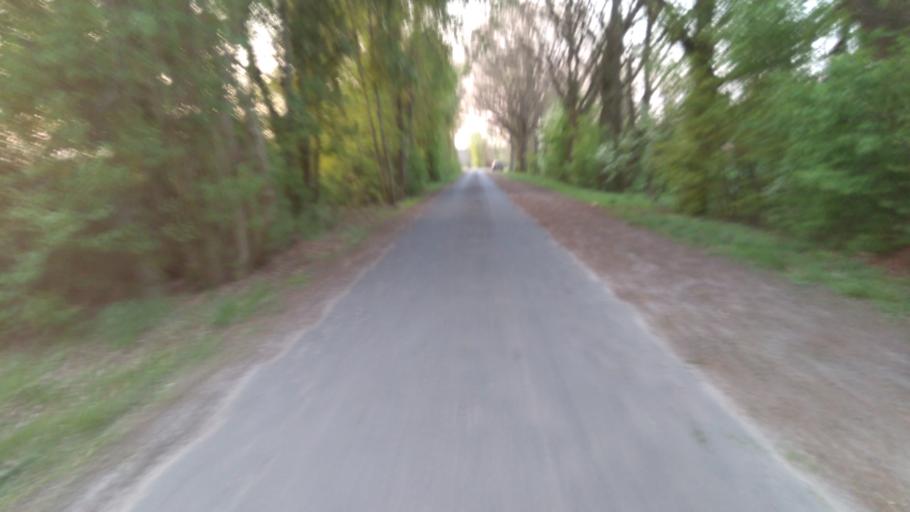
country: DE
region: Lower Saxony
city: Harsefeld
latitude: 53.4900
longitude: 9.5134
